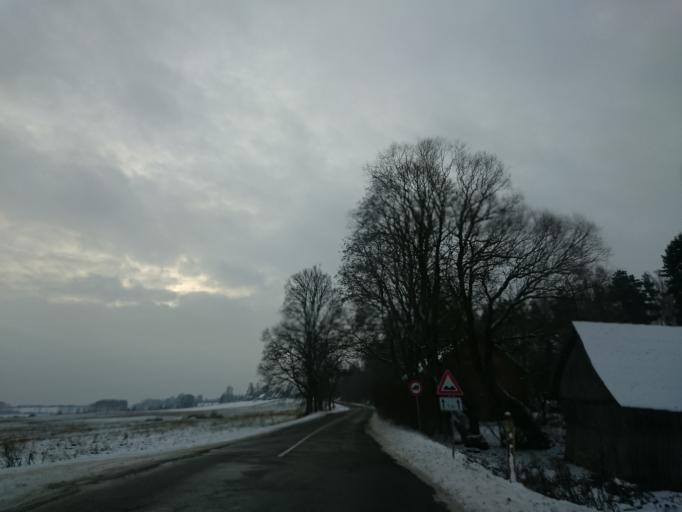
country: LV
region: Seja
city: Loja
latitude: 57.2116
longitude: 24.5866
